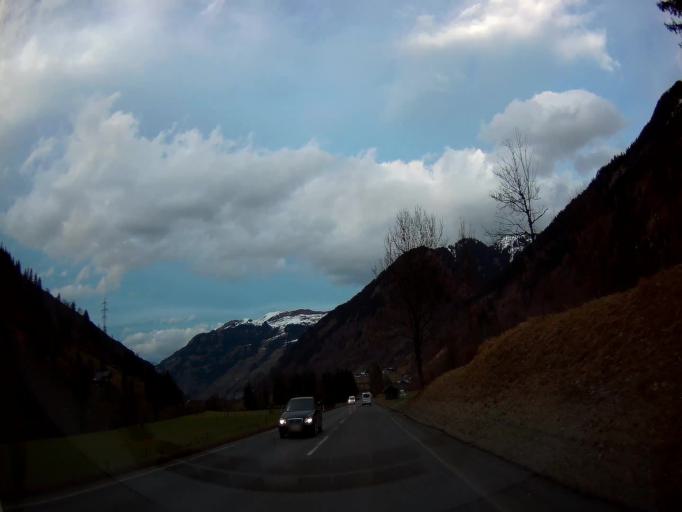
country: AT
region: Salzburg
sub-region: Politischer Bezirk Sankt Johann im Pongau
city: Bad Hofgastein
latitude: 47.2060
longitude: 13.1074
